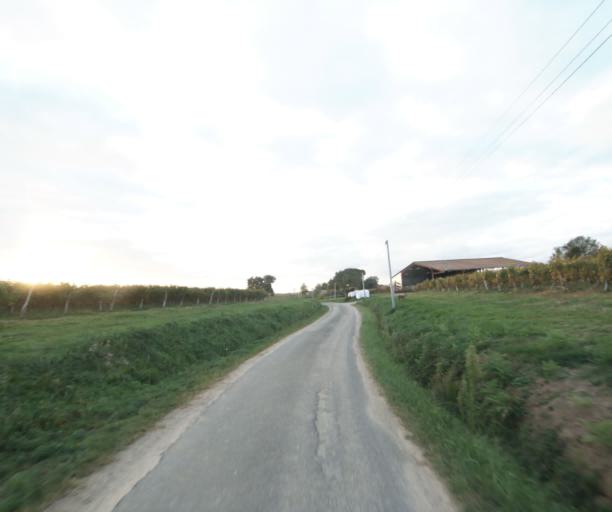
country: FR
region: Aquitaine
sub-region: Departement des Landes
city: Gabarret
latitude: 43.9759
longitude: 0.0905
